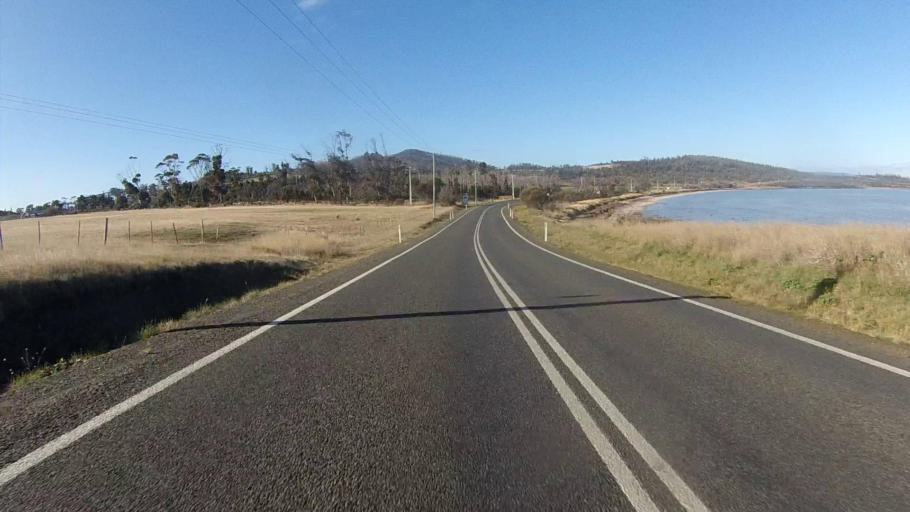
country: AU
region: Tasmania
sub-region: Sorell
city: Sorell
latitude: -42.8966
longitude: 147.8107
